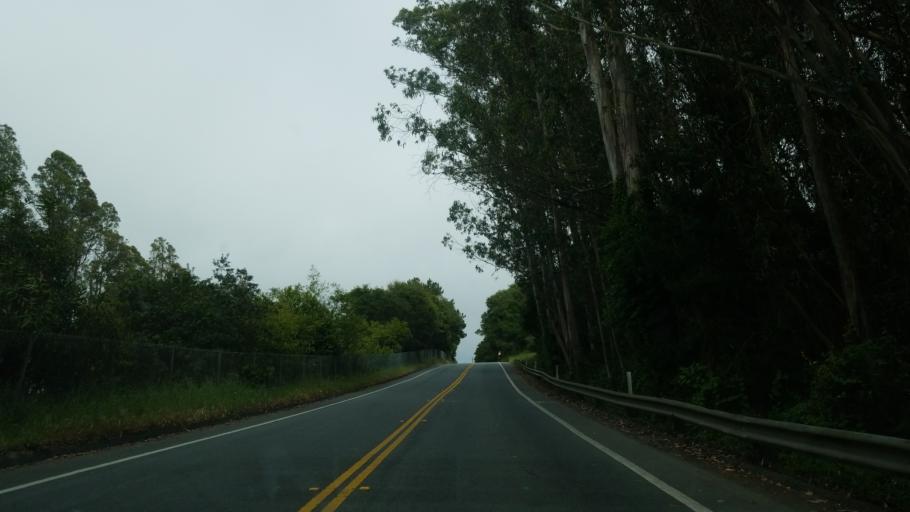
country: US
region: California
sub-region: Santa Cruz County
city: Seacliff
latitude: 36.9836
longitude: -121.9317
